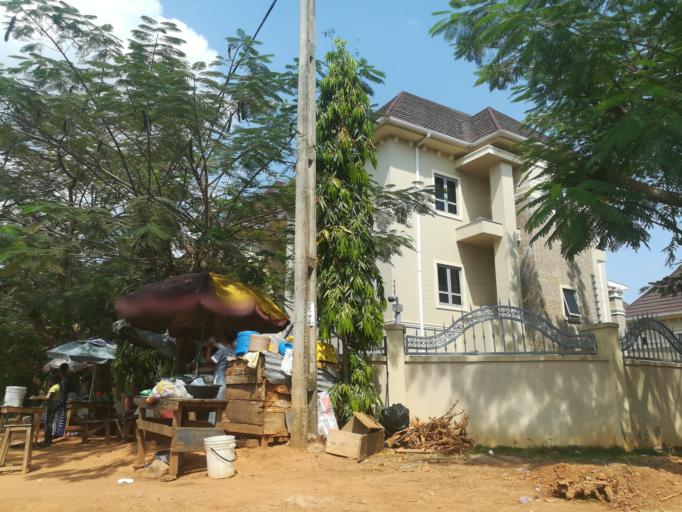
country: NG
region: Abuja Federal Capital Territory
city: Abuja
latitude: 9.0514
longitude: 7.4463
